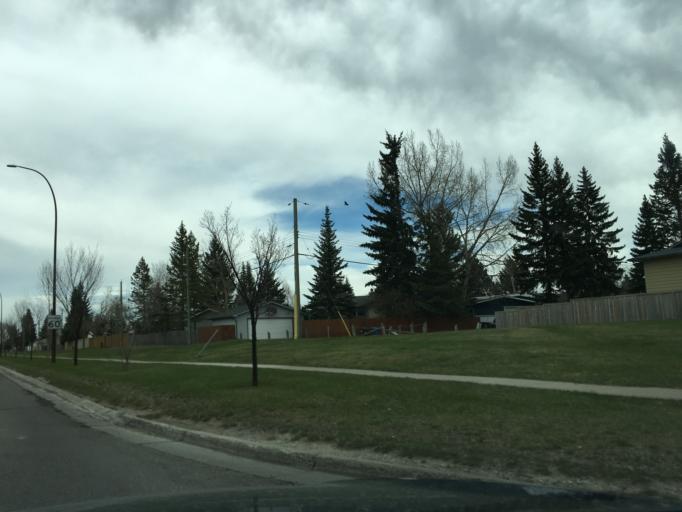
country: CA
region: Alberta
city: Calgary
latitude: 50.9613
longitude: -114.1323
